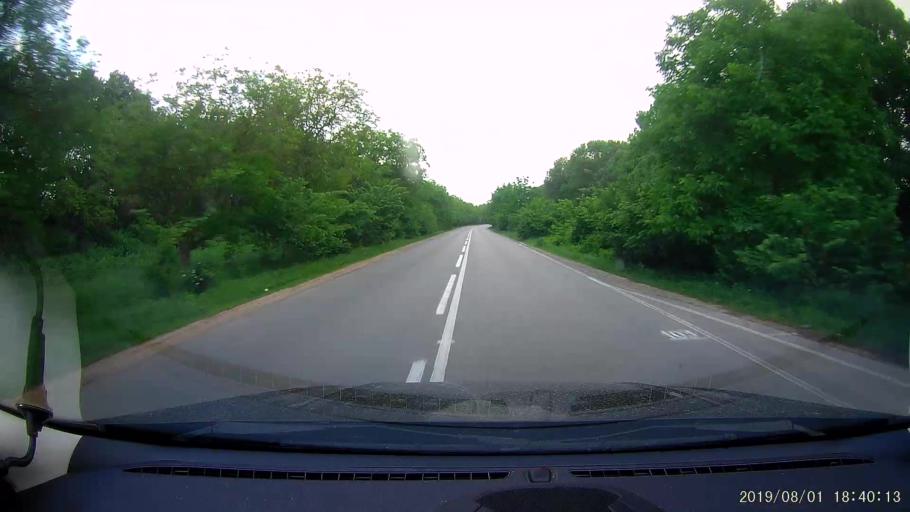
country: BG
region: Shumen
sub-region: Obshtina Khitrino
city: Gara Khitrino
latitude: 43.3714
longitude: 26.9200
